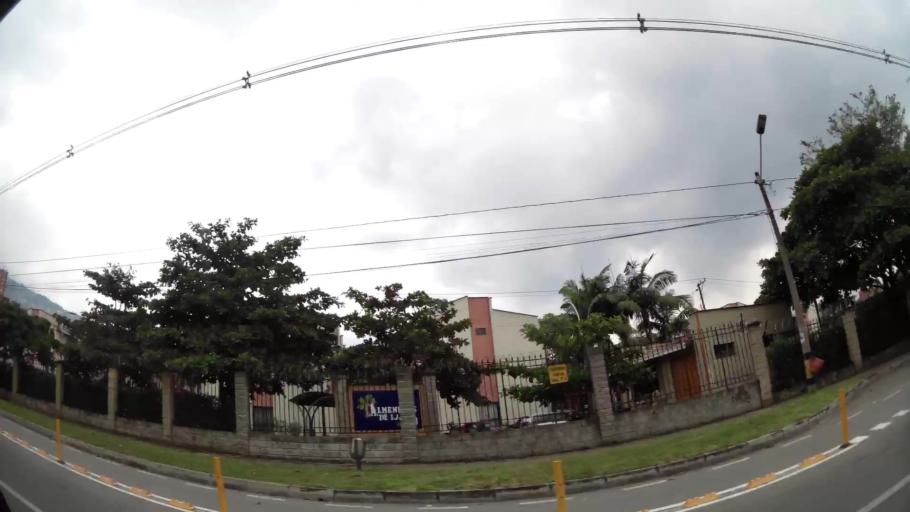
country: CO
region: Antioquia
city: Medellin
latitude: 6.2713
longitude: -75.5932
